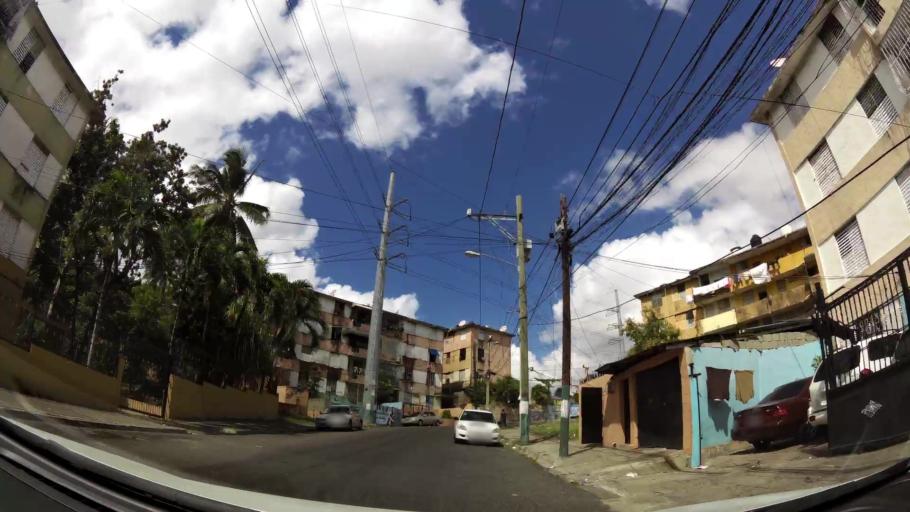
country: DO
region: Nacional
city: San Carlos
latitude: 18.4887
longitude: -69.8855
